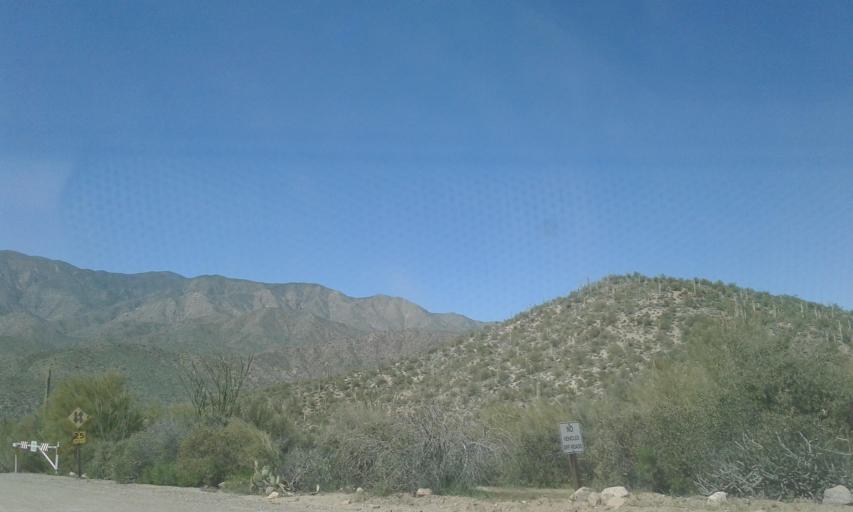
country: US
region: Arizona
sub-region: Gila County
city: Tonto Basin
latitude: 33.6238
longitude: -111.1964
